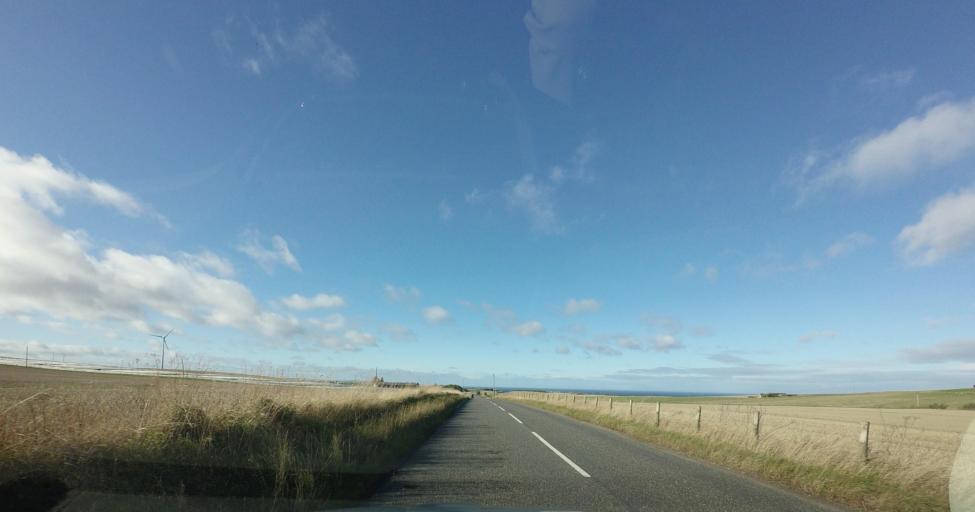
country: GB
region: Scotland
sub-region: Aberdeenshire
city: Macduff
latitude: 57.6620
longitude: -2.3683
